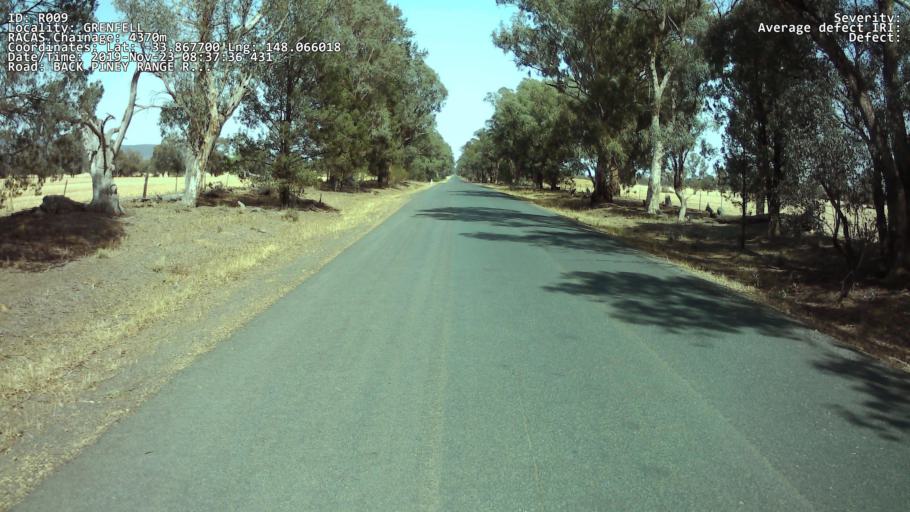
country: AU
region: New South Wales
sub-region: Weddin
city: Grenfell
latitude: -33.8677
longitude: 148.0660
